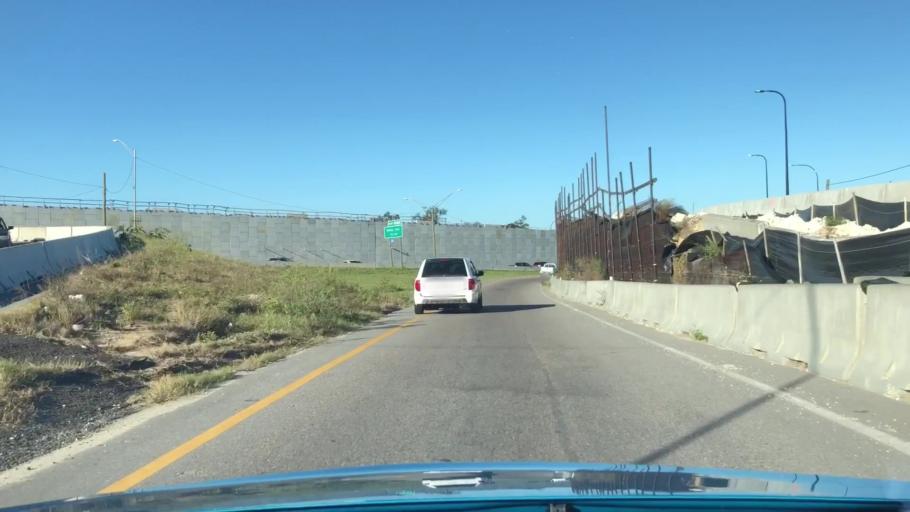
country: US
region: Florida
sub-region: Orange County
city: Holden Heights
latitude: 28.5098
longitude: -81.3956
